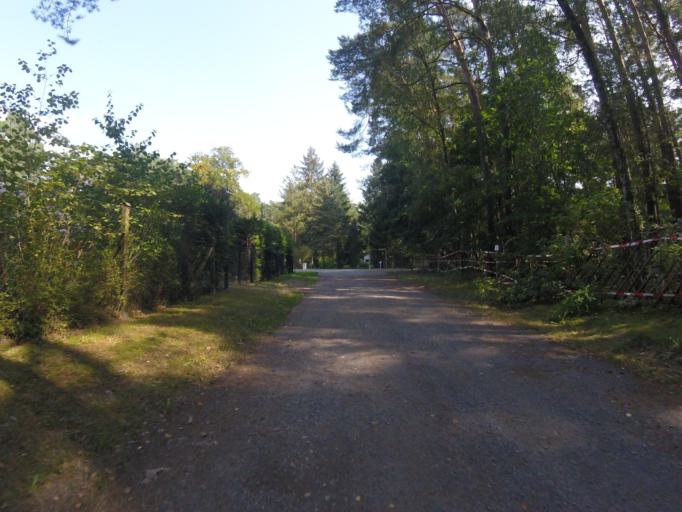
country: DE
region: Brandenburg
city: Bestensee
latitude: 52.2634
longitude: 13.7450
